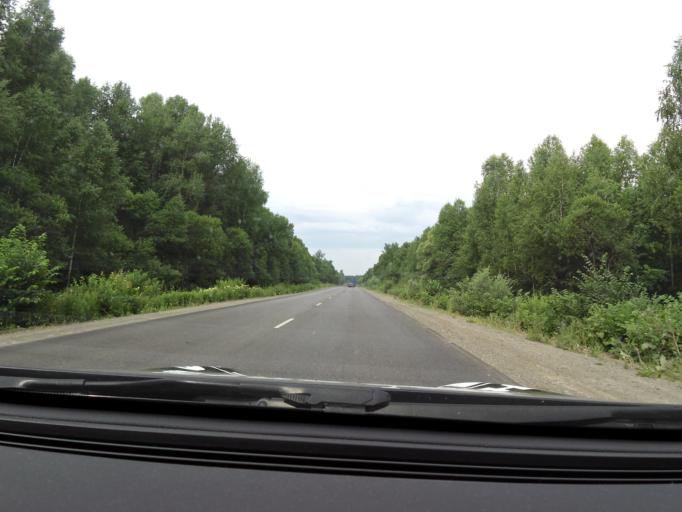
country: RU
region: Chelyabinsk
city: Asha
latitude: 54.8776
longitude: 57.2149
